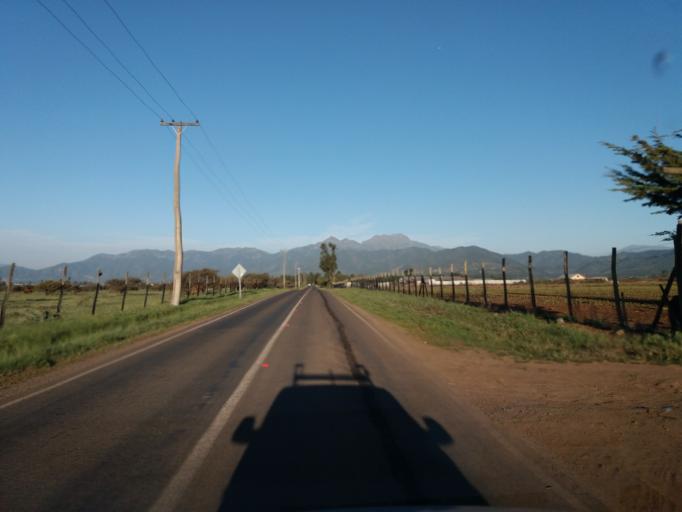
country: CL
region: Valparaiso
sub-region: Provincia de Quillota
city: Quillota
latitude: -32.9167
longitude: -71.3298
